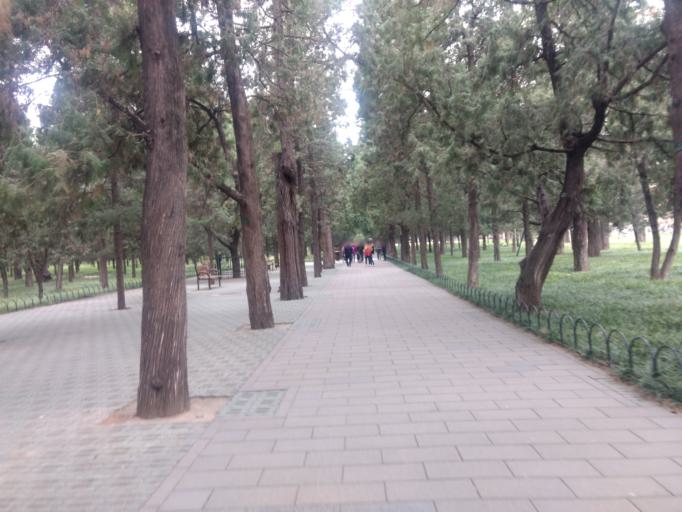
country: CN
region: Beijing
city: Longtan
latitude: 39.8766
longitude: 116.4046
